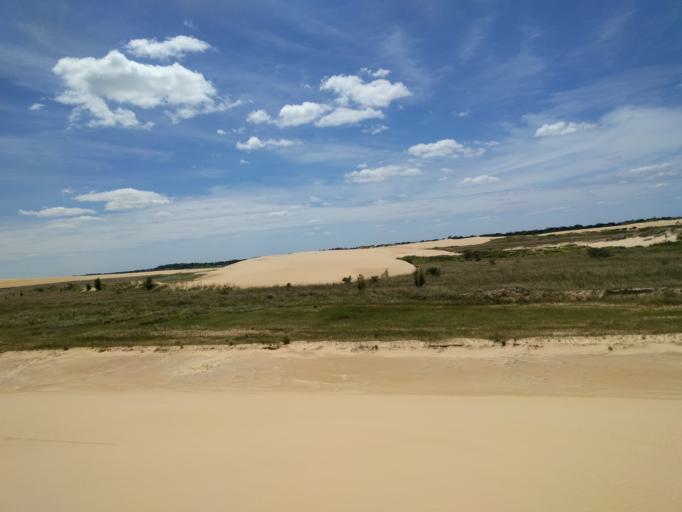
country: BO
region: Santa Cruz
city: Santa Cruz de la Sierra
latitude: -17.9514
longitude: -63.1518
